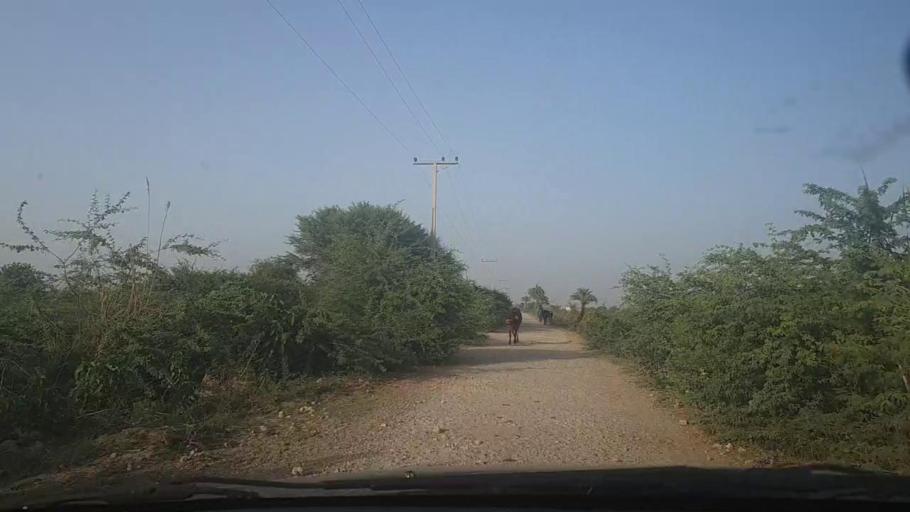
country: PK
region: Sindh
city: Keti Bandar
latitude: 24.2871
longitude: 67.6048
